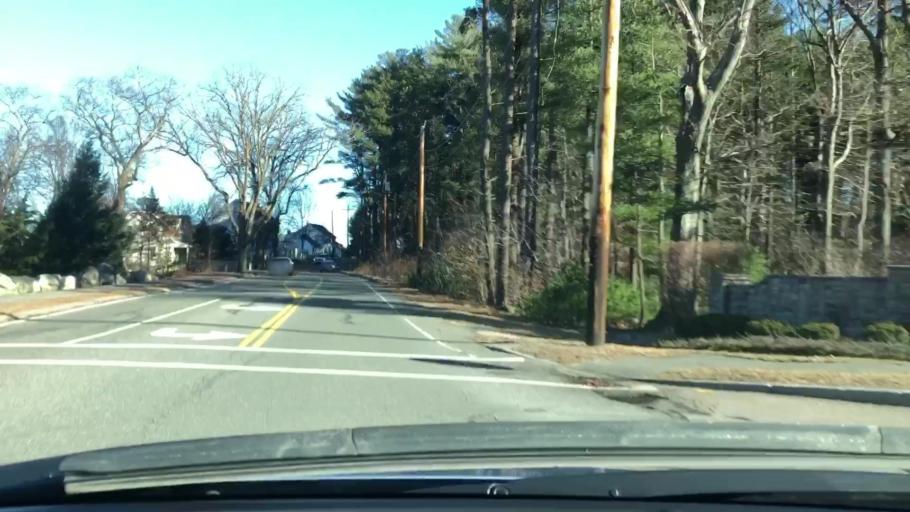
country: US
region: Massachusetts
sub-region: Norfolk County
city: Norwood
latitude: 42.1676
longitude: -71.2211
